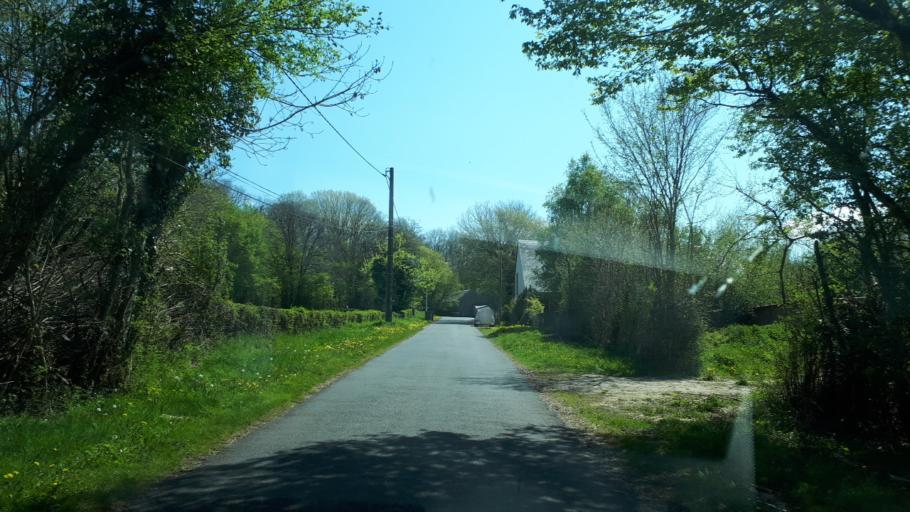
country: FR
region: Centre
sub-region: Departement du Cher
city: Henrichemont
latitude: 47.2983
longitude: 2.5786
